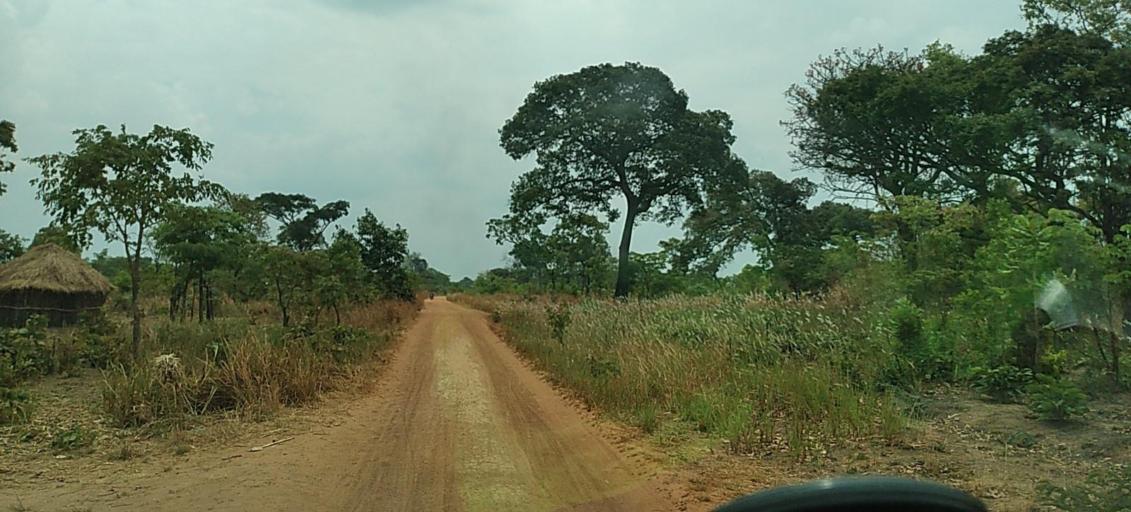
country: ZM
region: North-Western
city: Kansanshi
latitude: -12.0546
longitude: 26.3432
